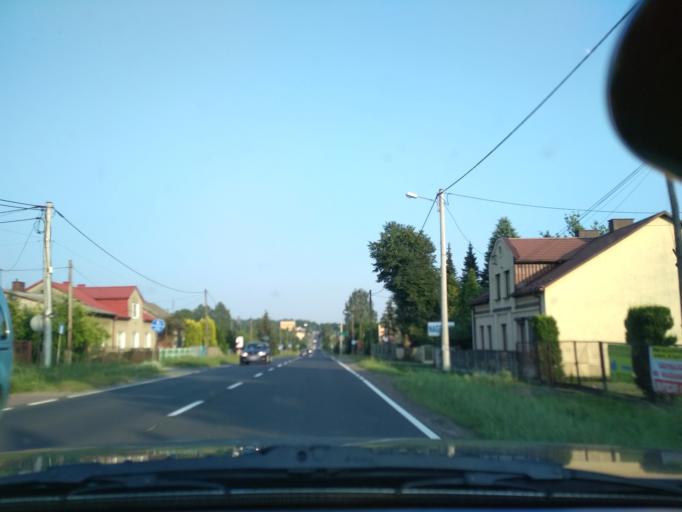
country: PL
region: Silesian Voivodeship
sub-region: Powiat zawiercianski
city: Ogrodzieniec
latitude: 50.4711
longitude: 19.4820
